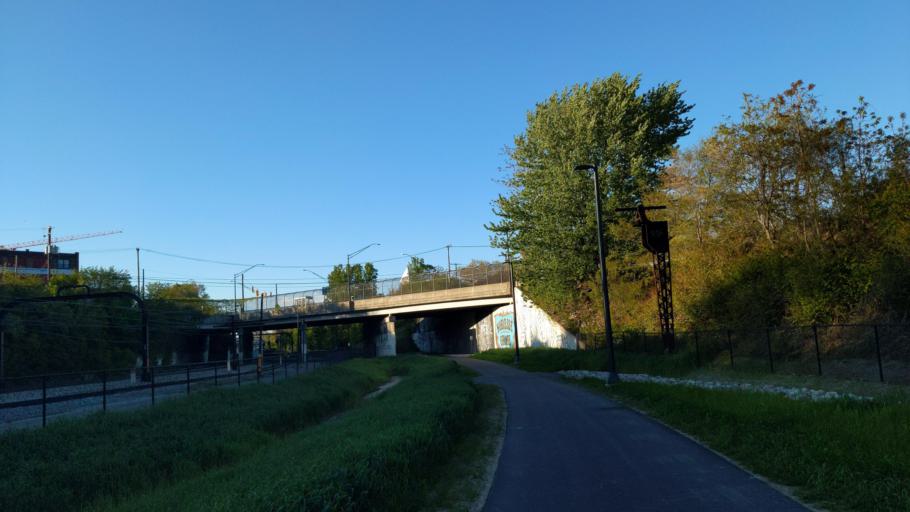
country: US
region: Ohio
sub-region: Cuyahoga County
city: Cleveland
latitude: 41.4801
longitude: -81.7012
